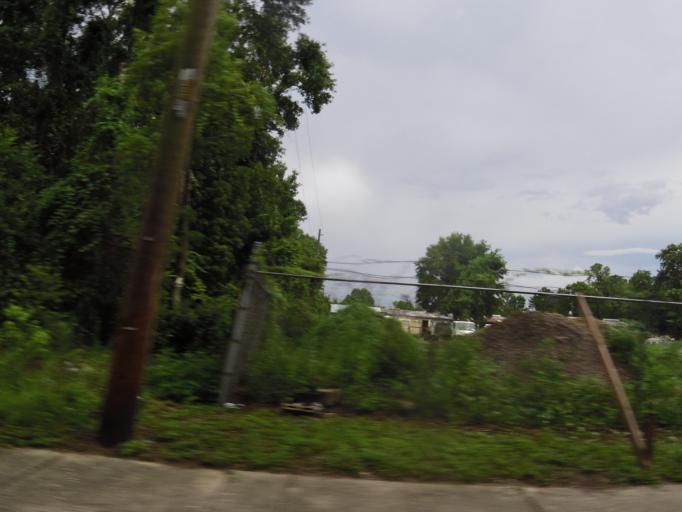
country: US
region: Florida
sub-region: Duval County
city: Jacksonville
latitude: 30.2766
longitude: -81.6379
